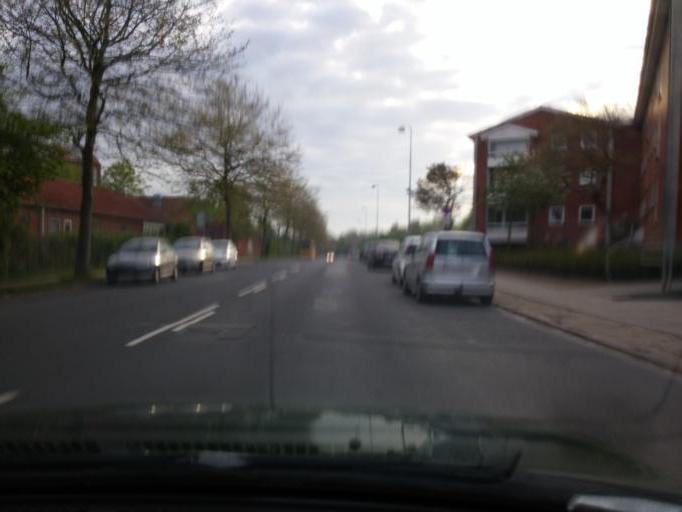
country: DK
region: South Denmark
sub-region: Odense Kommune
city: Odense
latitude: 55.3918
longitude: 10.4115
